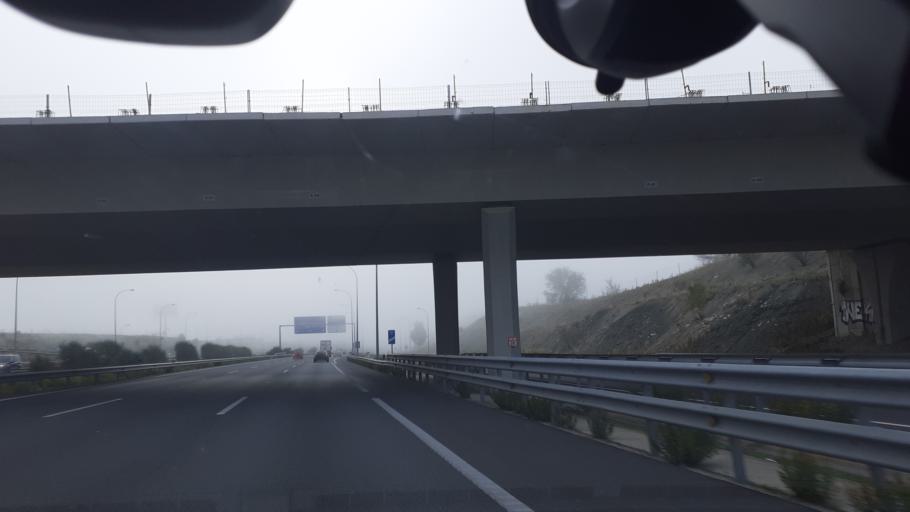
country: ES
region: Madrid
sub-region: Provincia de Madrid
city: Vicalvaro
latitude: 40.3832
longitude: -3.5882
